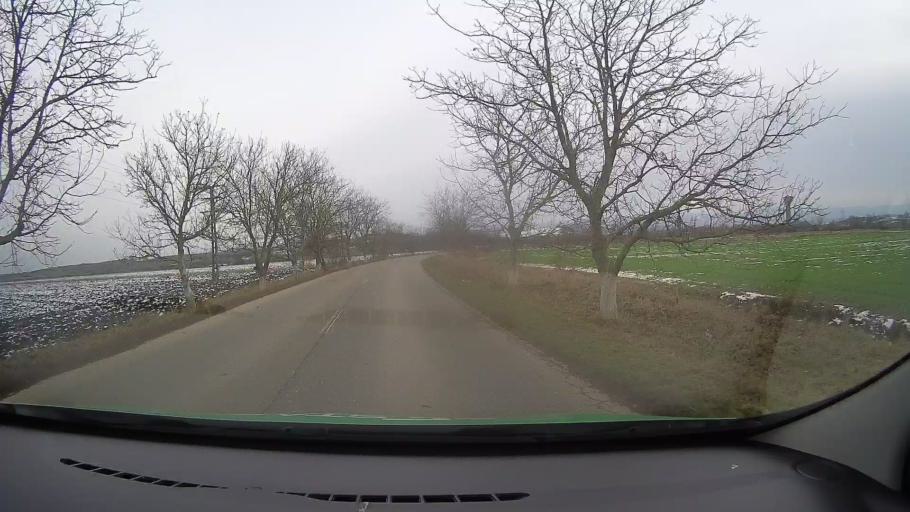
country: RO
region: Hunedoara
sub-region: Comuna Romos
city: Romos
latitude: 45.8820
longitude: 23.2545
